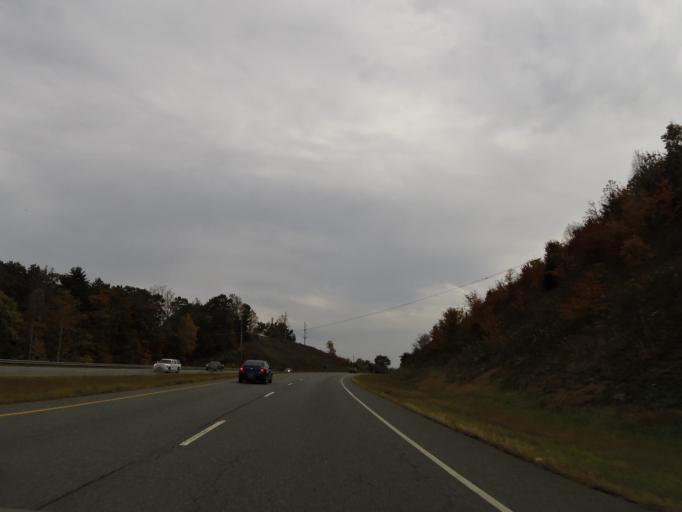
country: US
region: North Carolina
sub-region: Caldwell County
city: Lenoir
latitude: 36.0034
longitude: -81.5690
